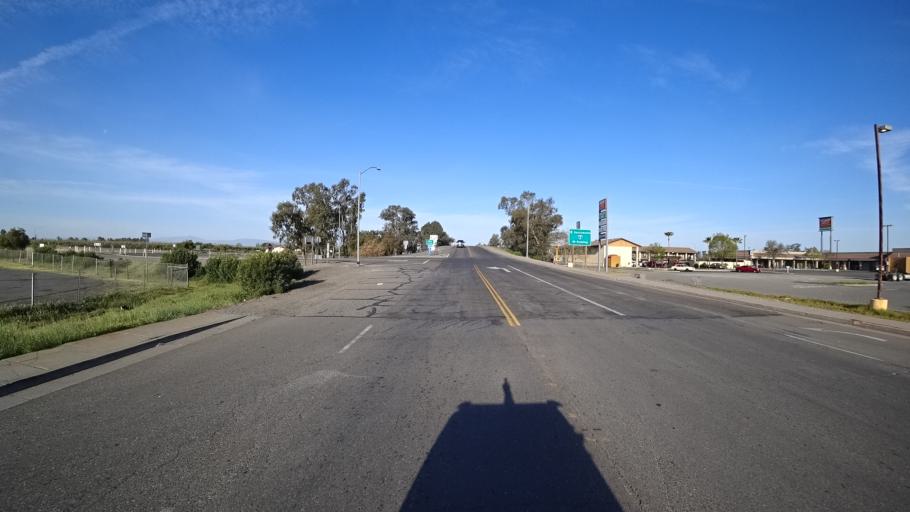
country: US
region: California
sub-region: Glenn County
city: Orland
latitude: 39.7403
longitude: -122.2035
